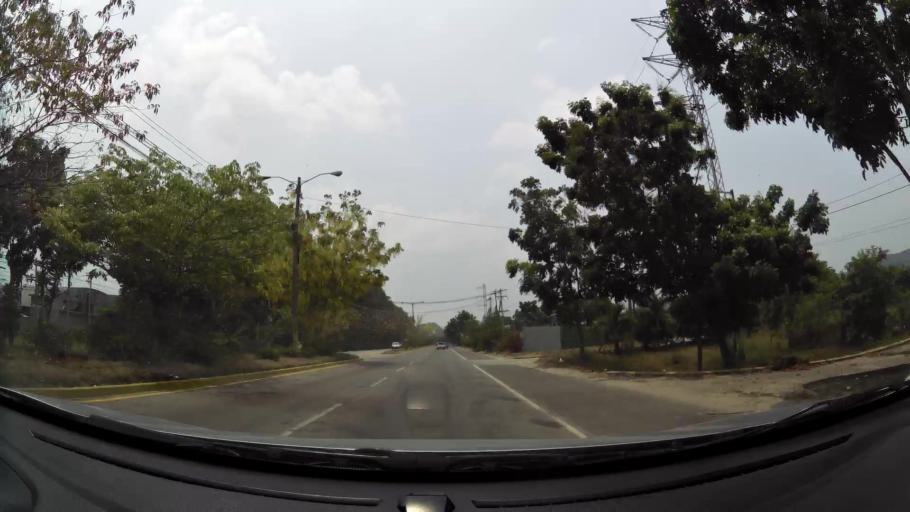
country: HN
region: Cortes
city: Chotepe
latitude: 15.4702
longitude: -87.9678
